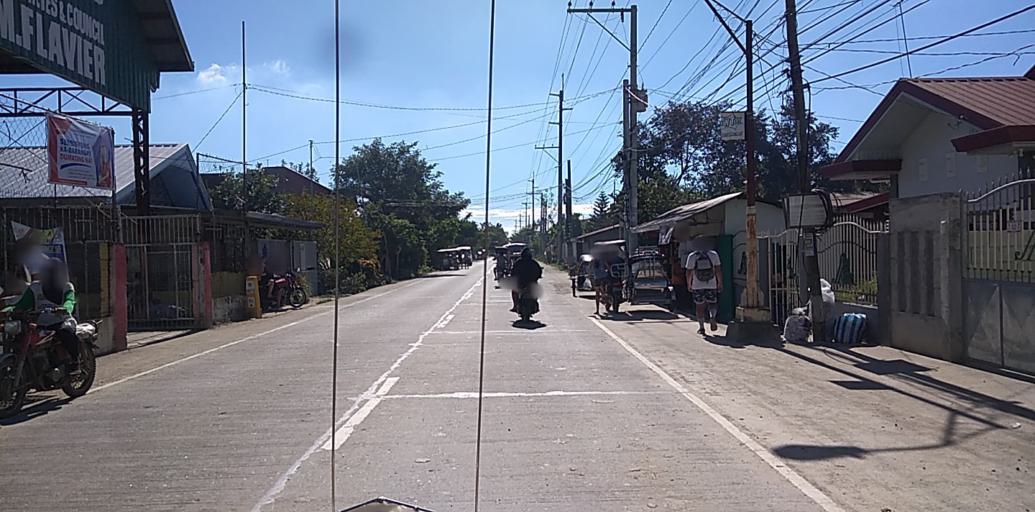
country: PH
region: Central Luzon
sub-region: Province of Pampanga
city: Santo Domingo
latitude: 15.0594
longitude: 120.7739
